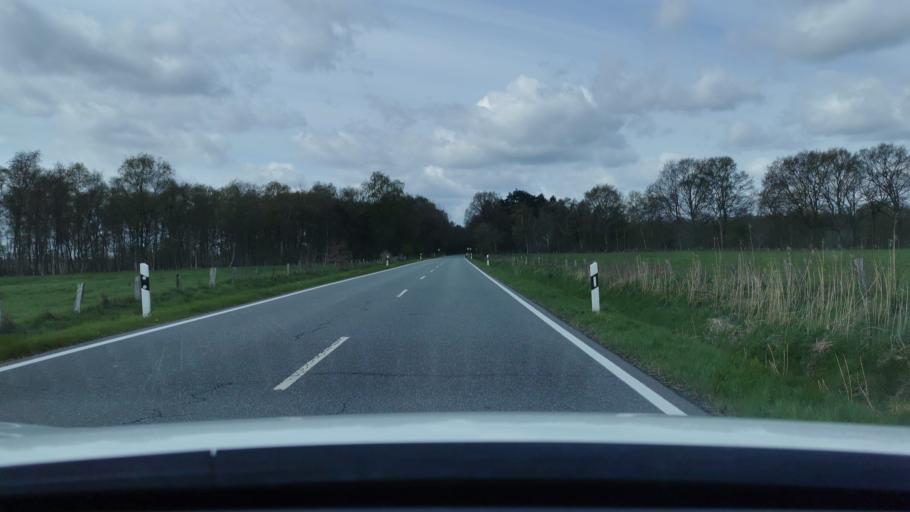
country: DE
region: Schleswig-Holstein
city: Tackesdorf
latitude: 54.1929
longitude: 9.4868
